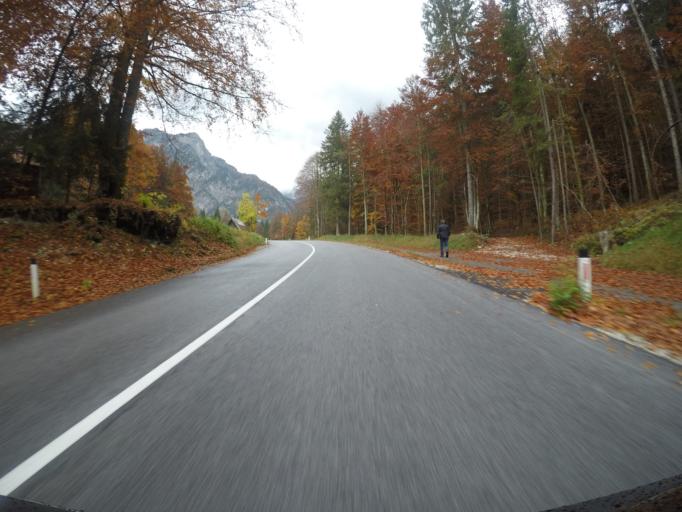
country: SI
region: Kranjska Gora
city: Kranjska Gora
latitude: 46.4829
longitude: 13.7228
